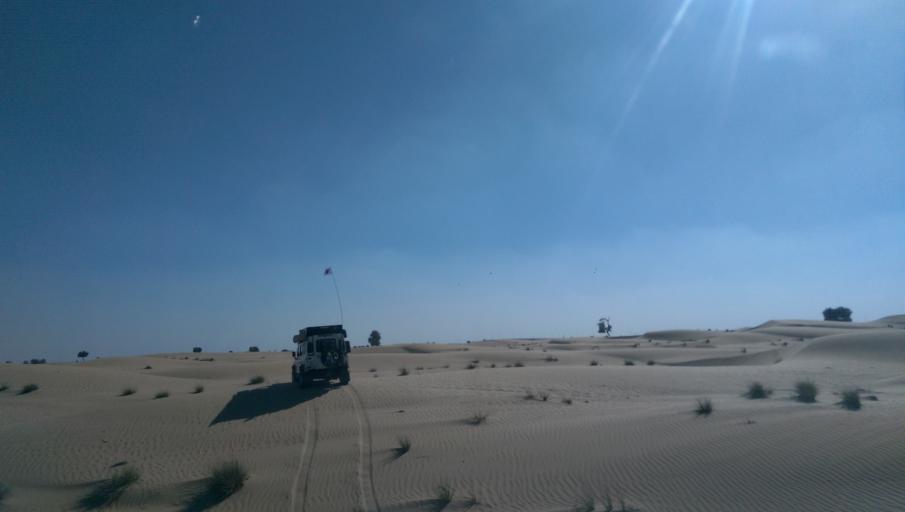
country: AE
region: Dubai
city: Dubai
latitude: 24.9643
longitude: 55.3477
